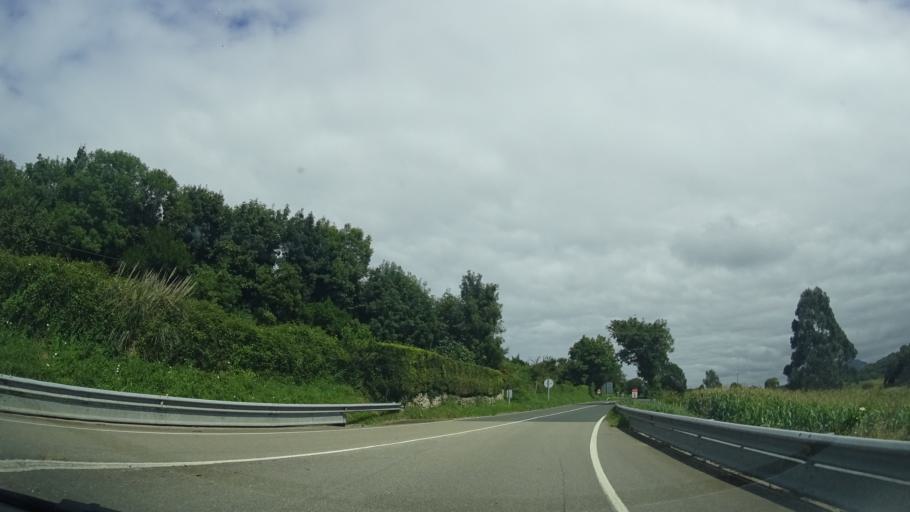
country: ES
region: Asturias
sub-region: Province of Asturias
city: Ribadesella
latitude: 43.4647
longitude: -5.1183
